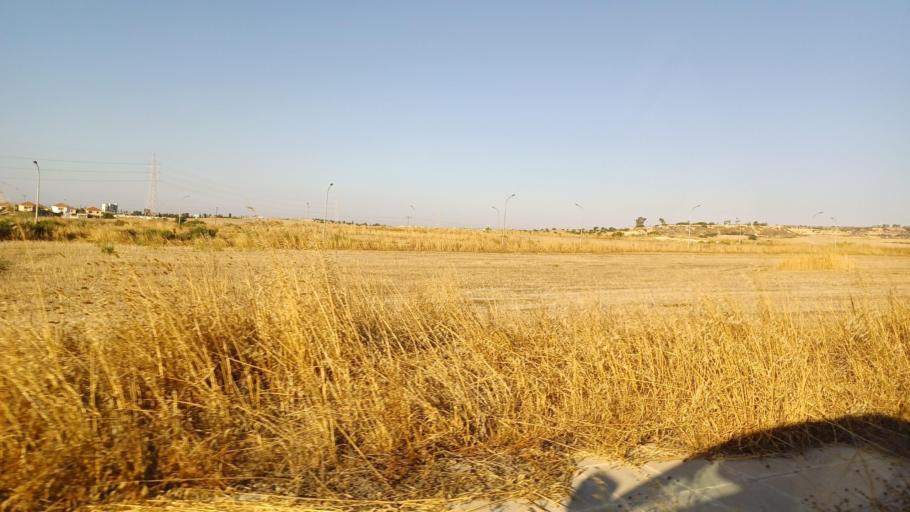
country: CY
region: Larnaka
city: Voroklini
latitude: 34.9909
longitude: 33.6777
